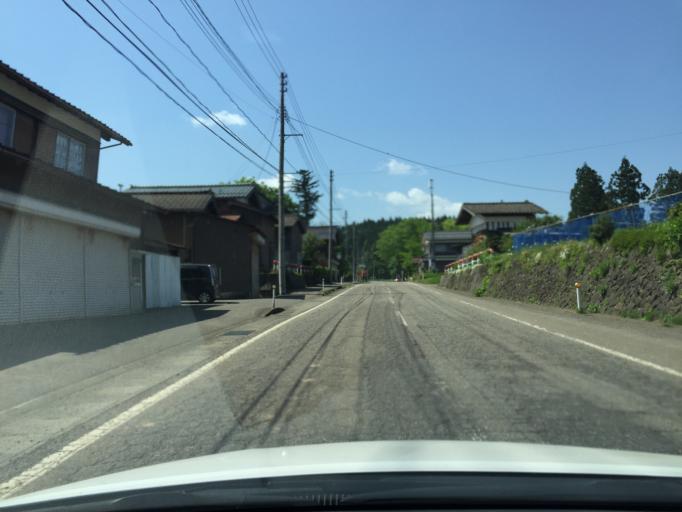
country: JP
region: Niigata
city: Tochio-honcho
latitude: 37.5419
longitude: 139.0933
